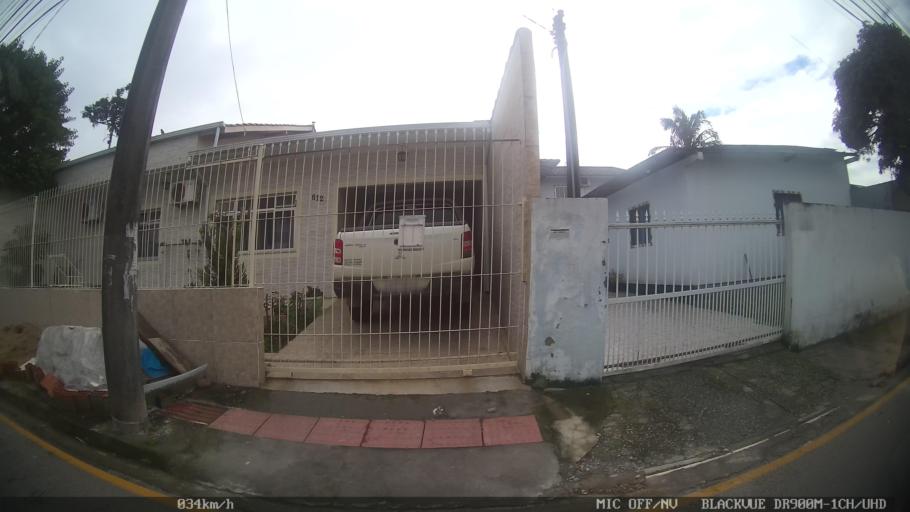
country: BR
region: Santa Catarina
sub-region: Sao Jose
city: Campinas
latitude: -27.5433
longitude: -48.6249
